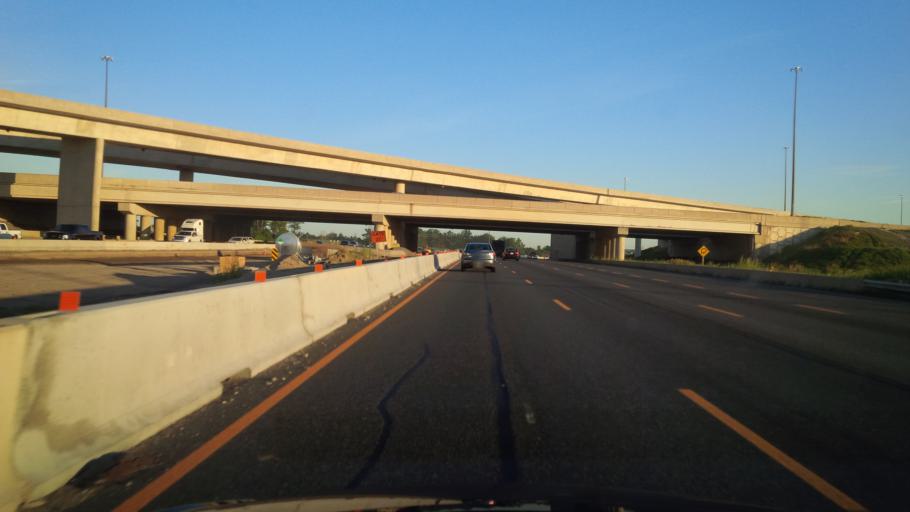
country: CA
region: Ontario
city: Brampton
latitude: 43.6679
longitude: -79.6986
